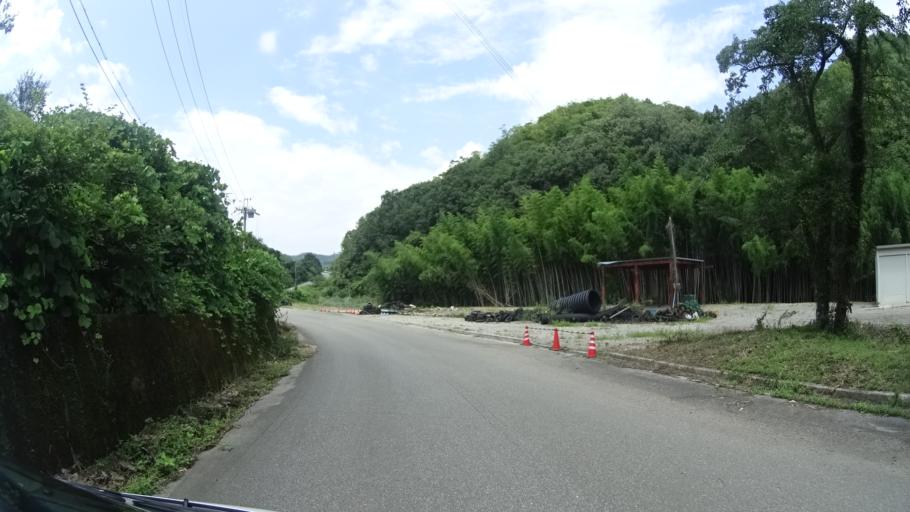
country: JP
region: Hyogo
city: Sasayama
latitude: 35.1668
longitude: 135.2658
